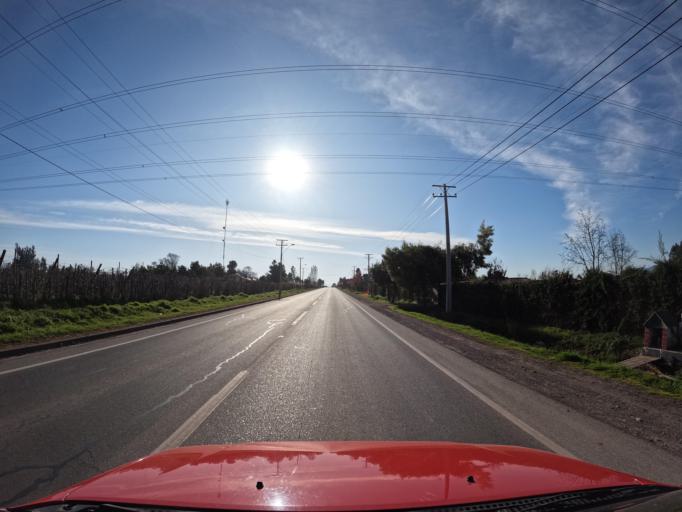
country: CL
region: Maule
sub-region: Provincia de Curico
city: Teno
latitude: -34.9505
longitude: -70.9870
